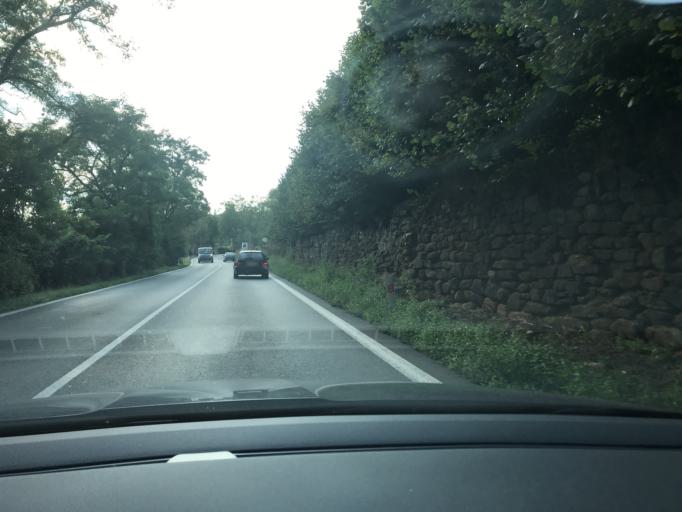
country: CZ
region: Central Bohemia
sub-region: Okres Kladno
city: Slany
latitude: 50.2355
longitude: 14.1023
